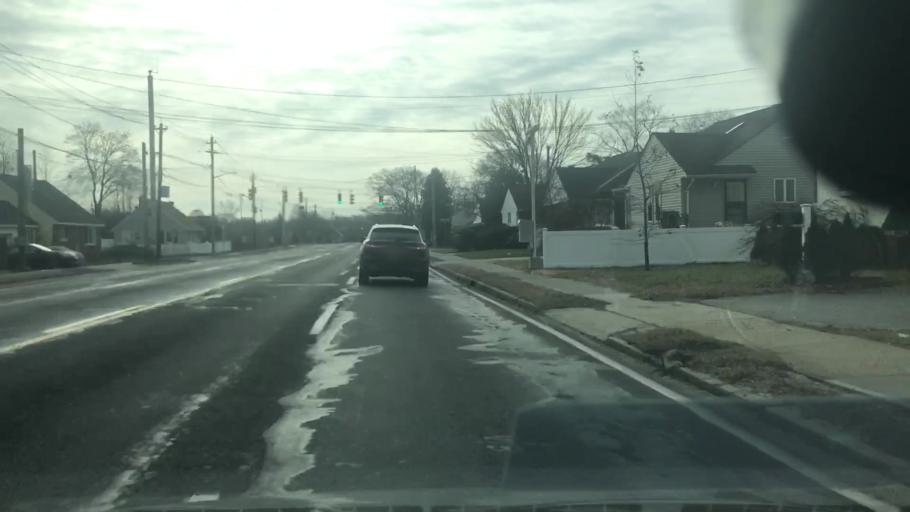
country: US
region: New York
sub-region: Suffolk County
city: Babylon
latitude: 40.6909
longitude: -73.3451
